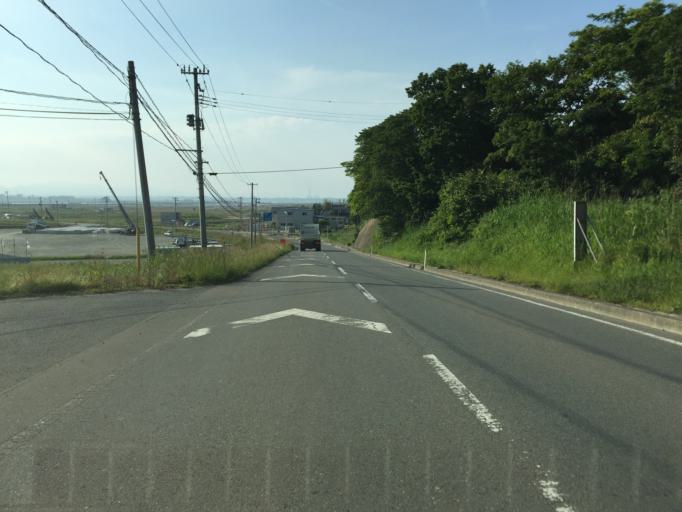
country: JP
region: Miyagi
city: Marumori
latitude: 37.7632
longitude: 140.9906
